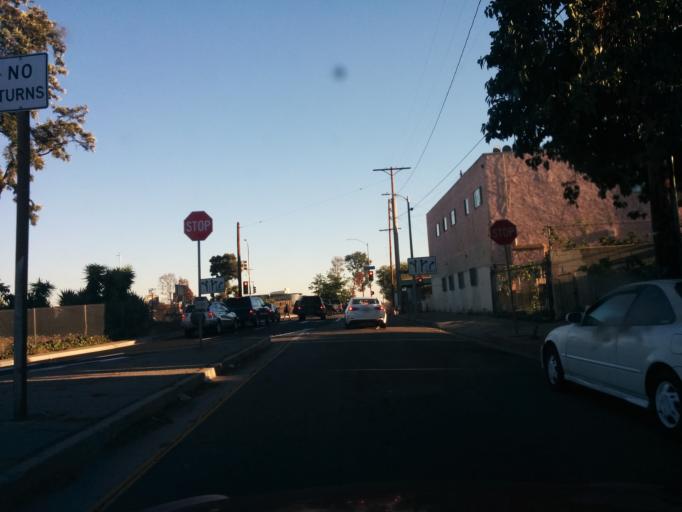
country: US
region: California
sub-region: Los Angeles County
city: Los Angeles
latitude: 34.0753
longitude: -118.2204
